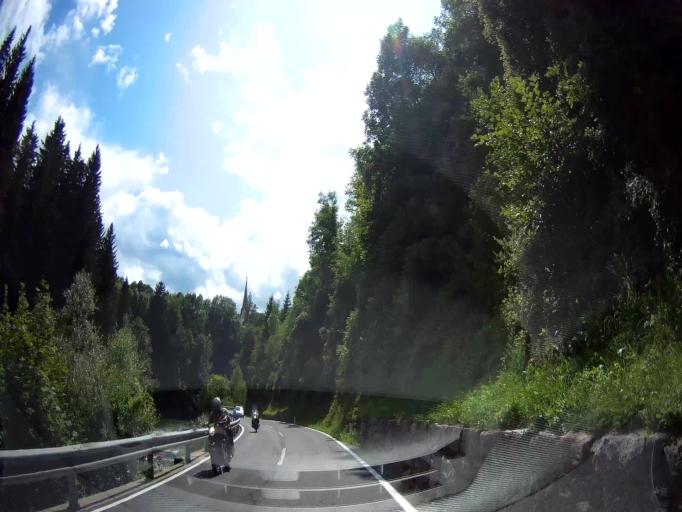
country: AT
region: Carinthia
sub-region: Politischer Bezirk Spittal an der Drau
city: Seeboden
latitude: 46.8349
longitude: 13.4945
